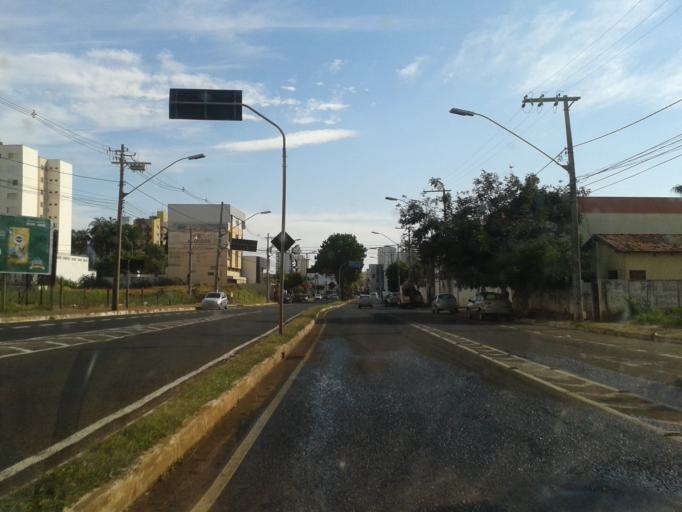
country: BR
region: Minas Gerais
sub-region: Uberlandia
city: Uberlandia
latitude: -18.9131
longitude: -48.2601
